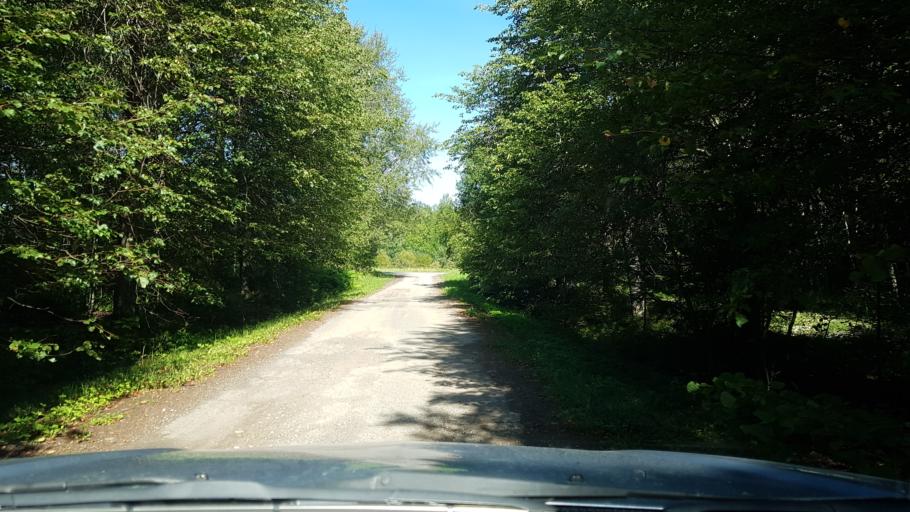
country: EE
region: Ida-Virumaa
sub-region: Sillamaee linn
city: Sillamae
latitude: 59.3478
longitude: 27.7368
